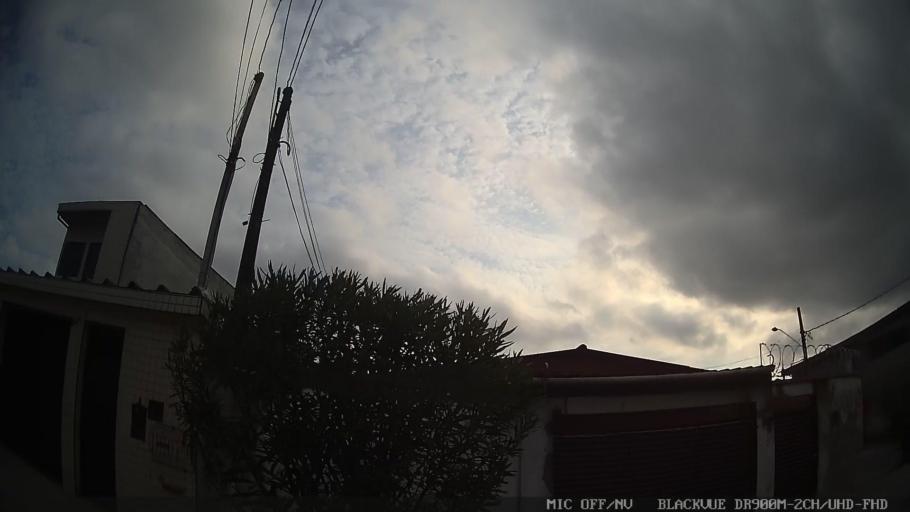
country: BR
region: Sao Paulo
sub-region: Guaruja
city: Guaruja
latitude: -23.9529
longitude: -46.2843
